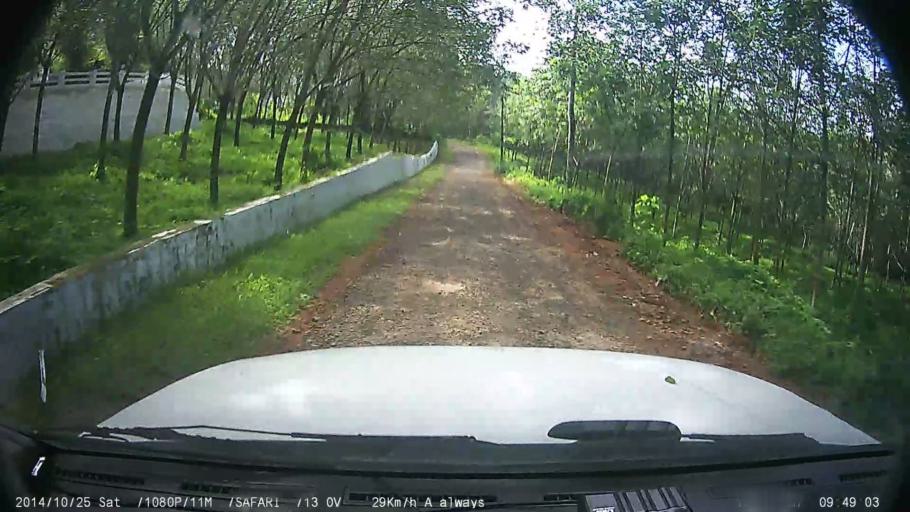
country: IN
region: Kerala
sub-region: Kottayam
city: Palackattumala
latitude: 9.7861
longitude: 76.5740
